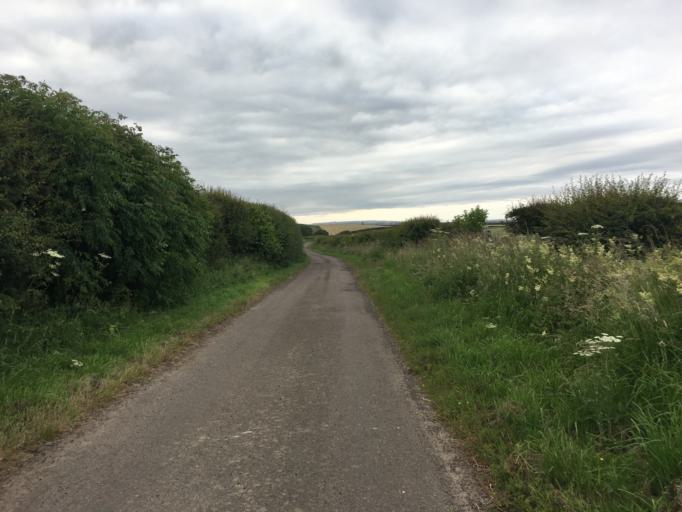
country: GB
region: England
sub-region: Northumberland
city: Lowick
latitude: 55.6568
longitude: -1.9036
